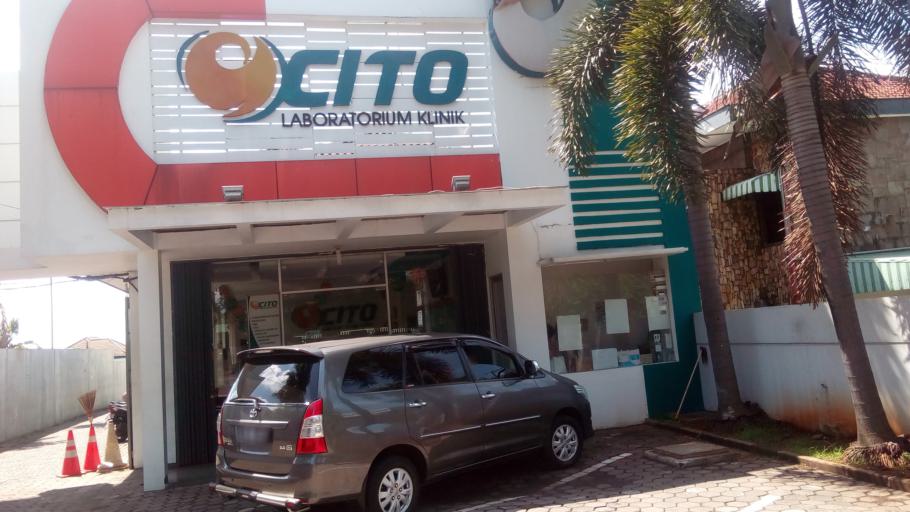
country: ID
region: Central Java
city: Semarang
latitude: -7.0549
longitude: 110.4158
